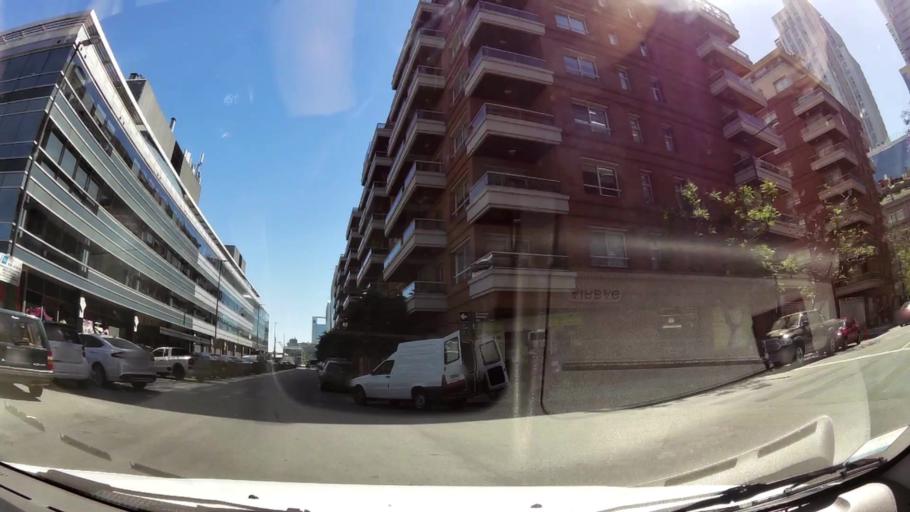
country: AR
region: Buenos Aires F.D.
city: Buenos Aires
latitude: -34.6107
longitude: -58.3635
